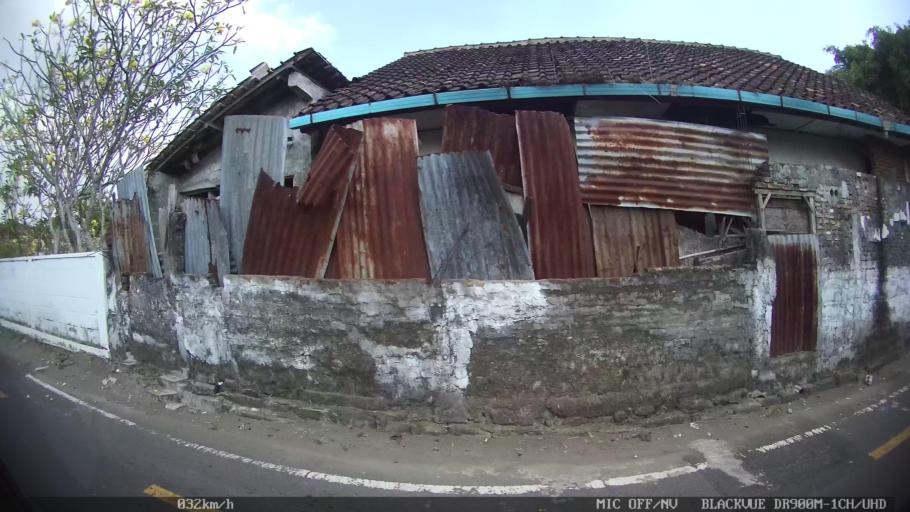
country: ID
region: Daerah Istimewa Yogyakarta
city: Yogyakarta
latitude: -7.8224
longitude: 110.3967
